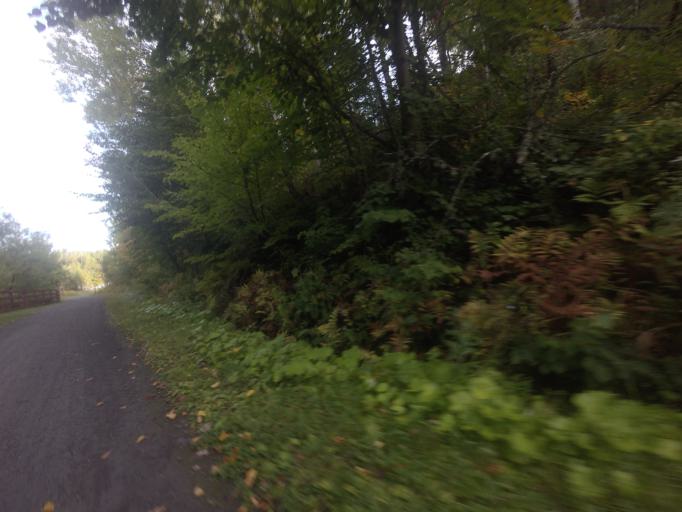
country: CA
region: Quebec
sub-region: Laurentides
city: Sainte-Adele
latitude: 45.9352
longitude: -74.1229
